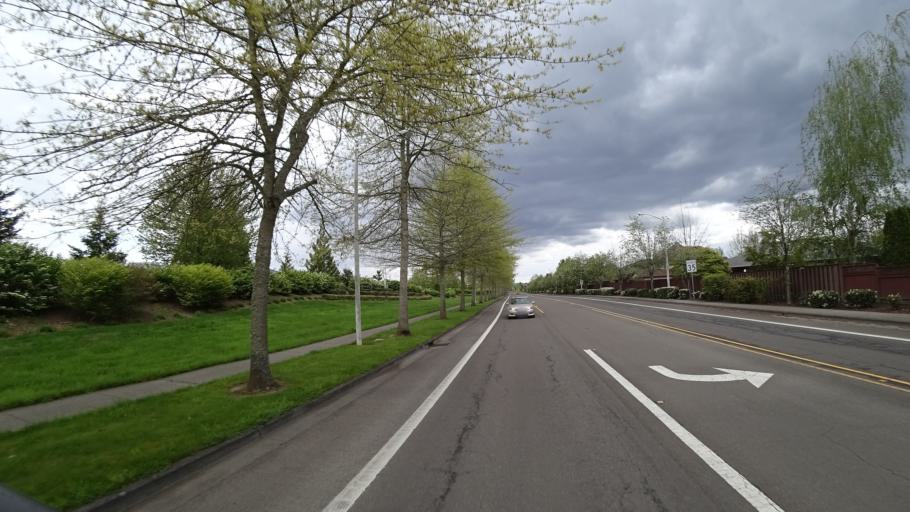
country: US
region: Oregon
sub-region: Washington County
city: Rockcreek
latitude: 45.5382
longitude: -122.9244
